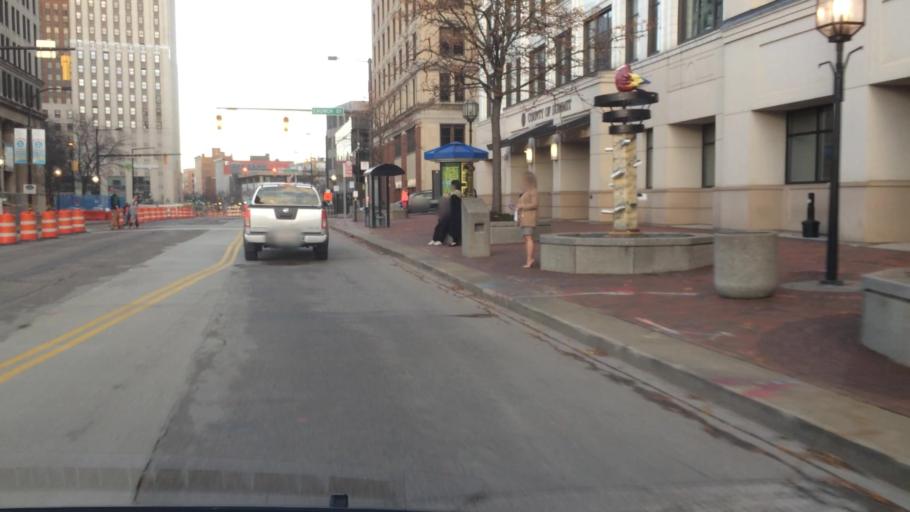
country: US
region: Ohio
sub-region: Summit County
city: Akron
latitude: 41.0803
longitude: -81.5194
